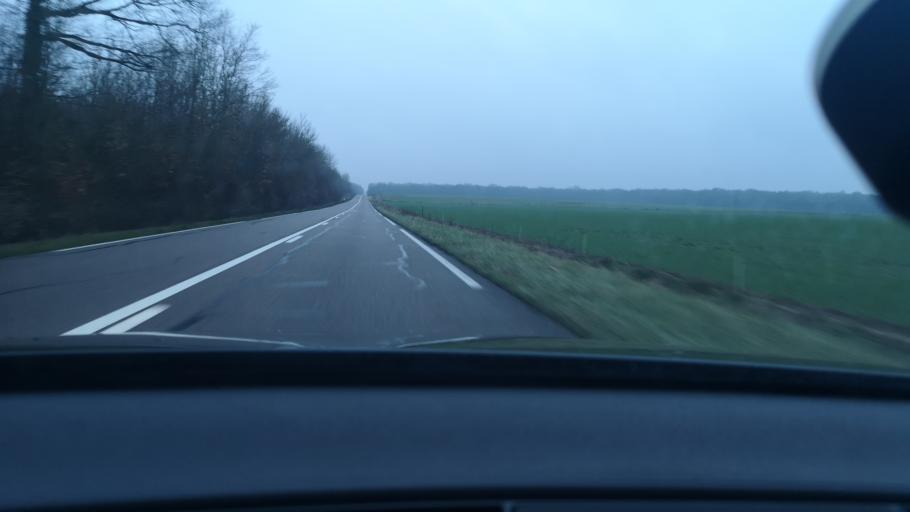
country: FR
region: Bourgogne
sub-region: Departement de la Cote-d'Or
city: Aiserey
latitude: 47.1199
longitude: 5.0996
